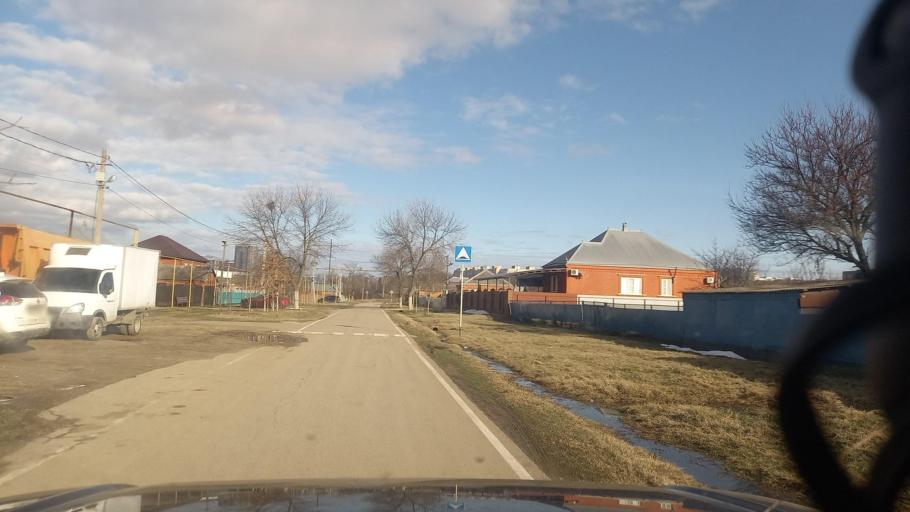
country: RU
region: Adygeya
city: Yablonovskiy
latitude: 45.0339
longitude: 38.8956
